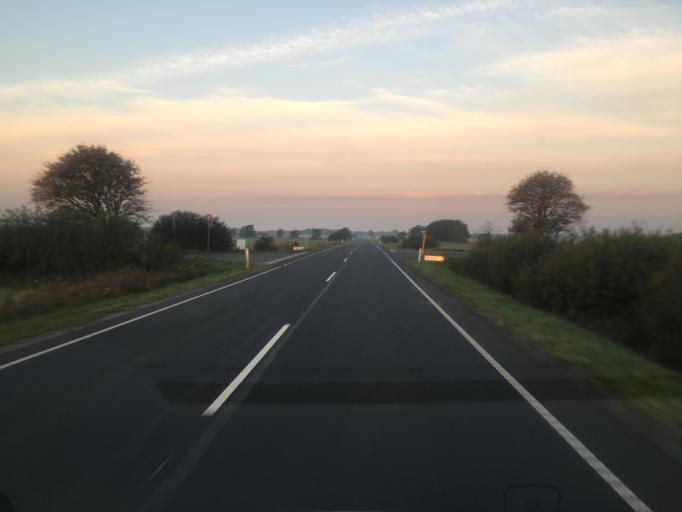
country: DE
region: Schleswig-Holstein
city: Bramstedtlund
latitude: 54.9729
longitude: 9.0700
